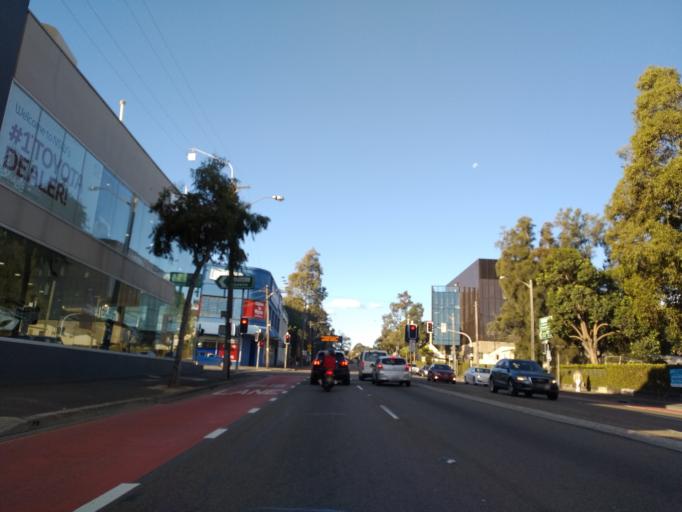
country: AU
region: New South Wales
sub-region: Marrickville
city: Camperdown
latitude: -33.8852
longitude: 151.1840
